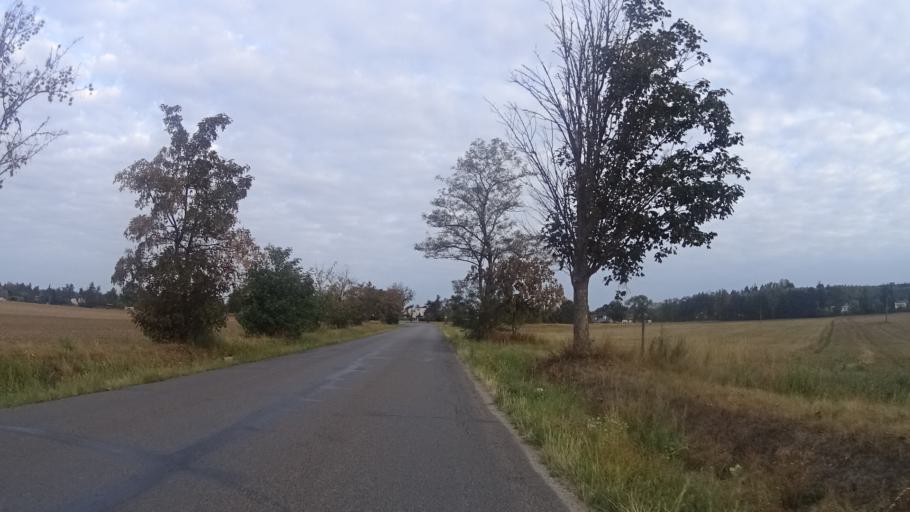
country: CZ
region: Kralovehradecky
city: Cernilov
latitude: 50.2122
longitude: 15.9126
